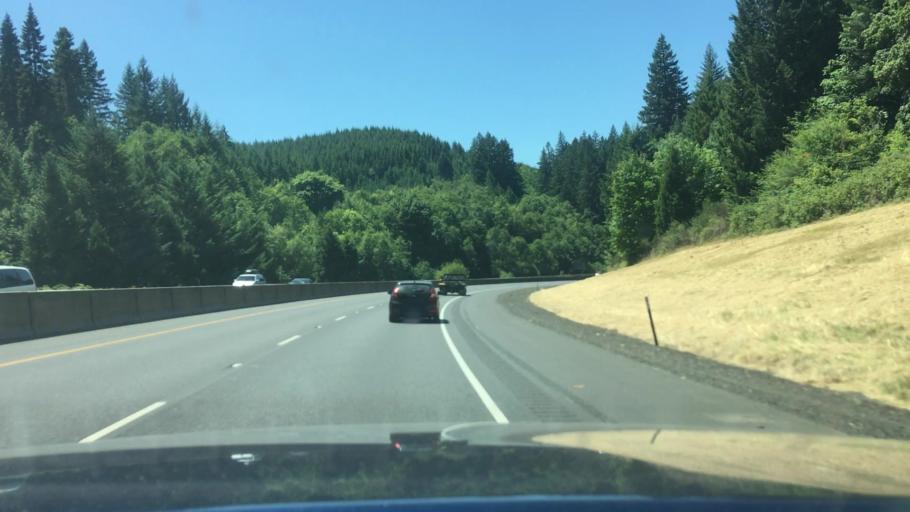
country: US
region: Oregon
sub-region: Lane County
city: Cottage Grove
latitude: 43.7518
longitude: -123.1450
